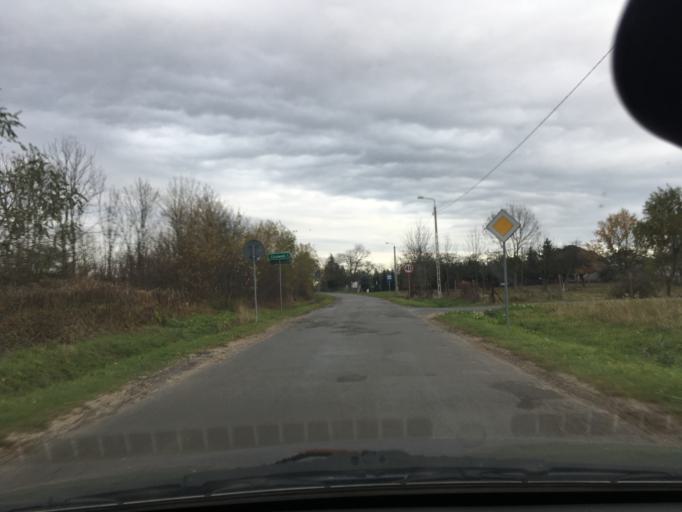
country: PL
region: Lodz Voivodeship
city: Zabia Wola
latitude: 52.0109
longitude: 20.7020
